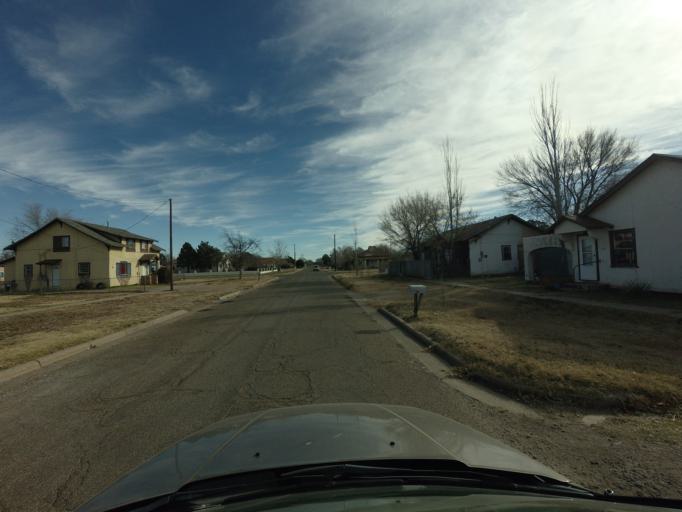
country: US
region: New Mexico
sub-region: Curry County
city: Clovis
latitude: 34.4068
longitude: -103.2034
